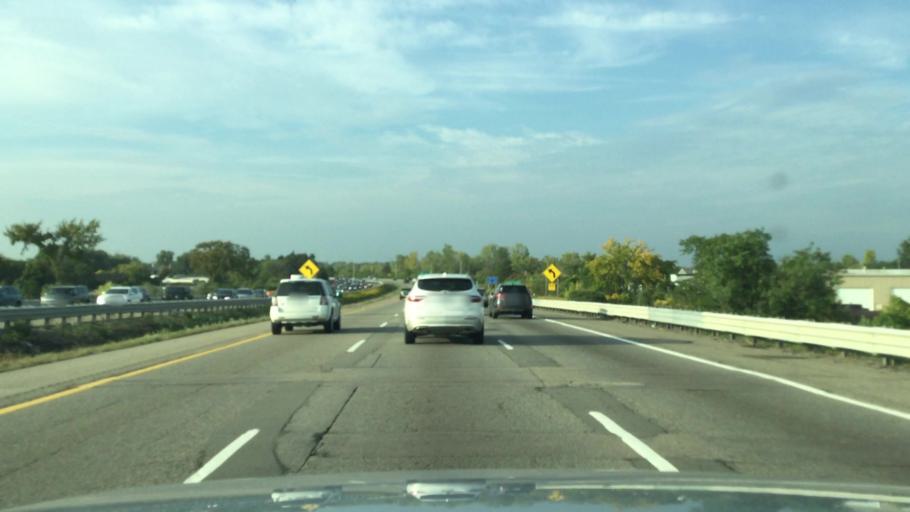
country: US
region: Michigan
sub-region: Oakland County
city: Clawson
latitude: 42.5502
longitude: -83.1166
